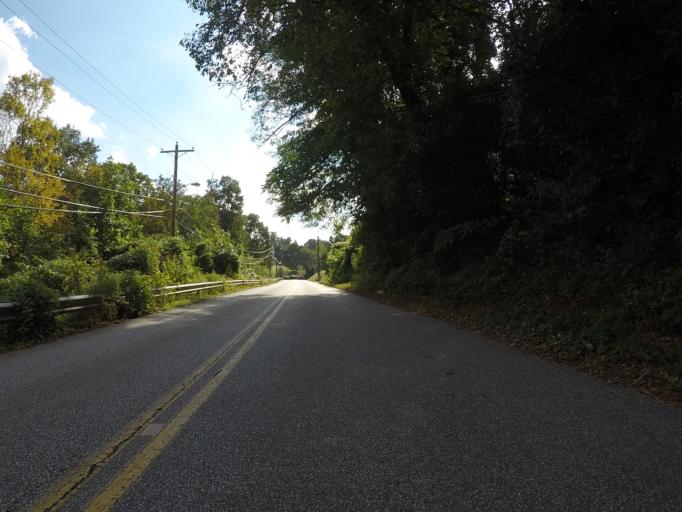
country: US
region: West Virginia
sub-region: Cabell County
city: Huntington
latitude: 38.4028
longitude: -82.4388
